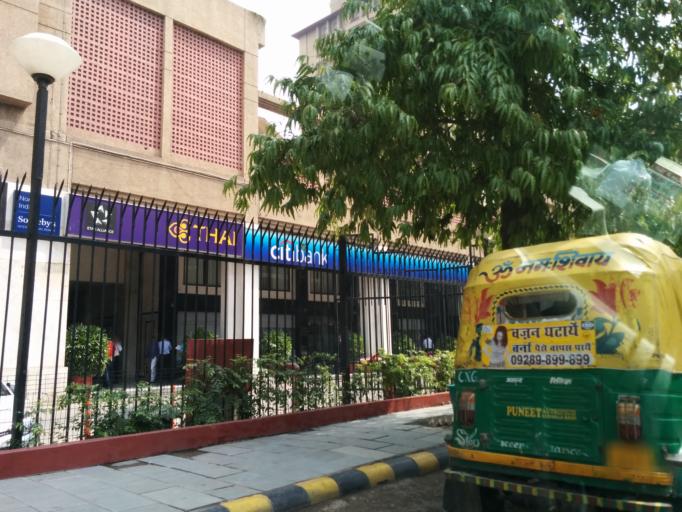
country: IN
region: Uttar Pradesh
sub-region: Gautam Buddha Nagar
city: Noida
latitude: 28.5498
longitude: 77.2494
